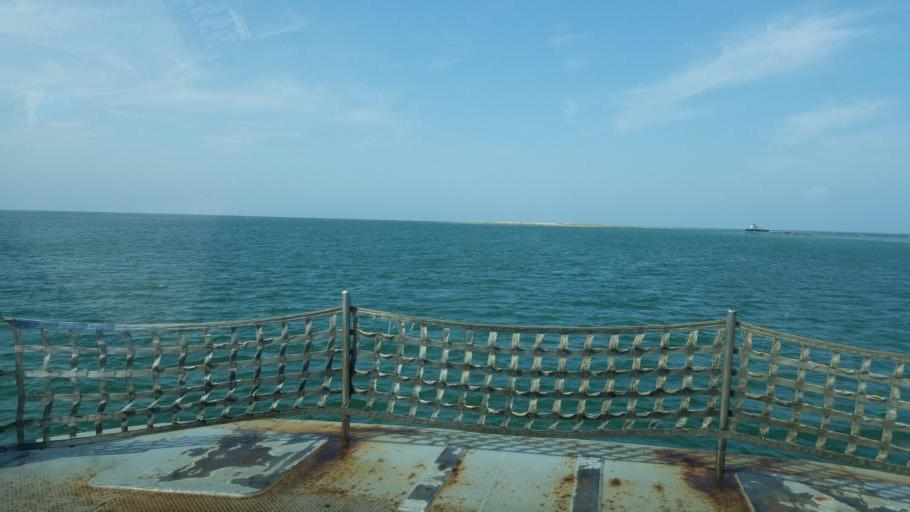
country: US
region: North Carolina
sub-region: Dare County
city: Buxton
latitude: 35.2060
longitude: -75.7224
